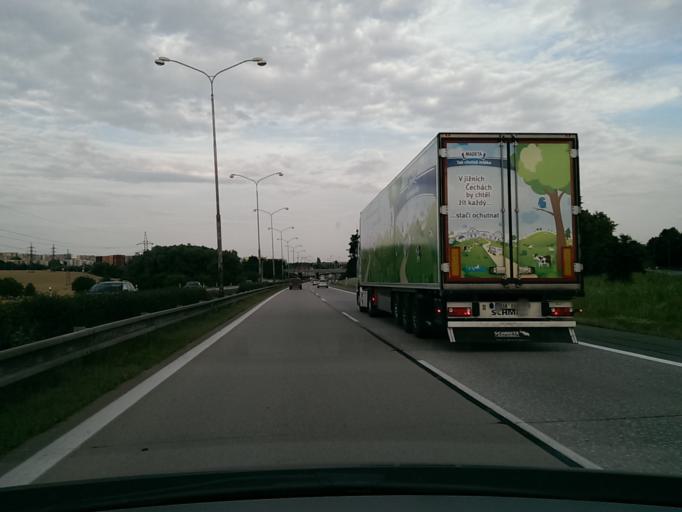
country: CZ
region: South Moravian
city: Ostopovice
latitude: 49.1688
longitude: 16.5383
